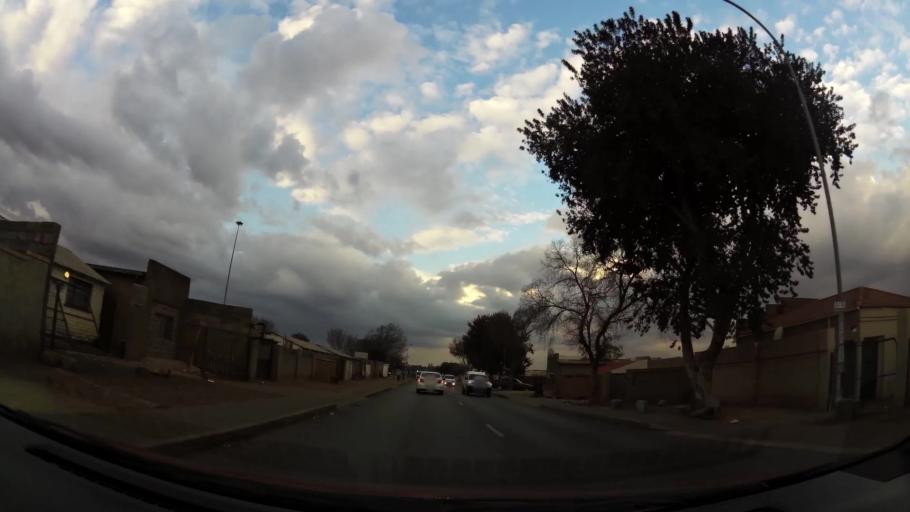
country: ZA
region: Gauteng
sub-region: City of Johannesburg Metropolitan Municipality
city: Soweto
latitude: -26.2421
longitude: 27.8376
